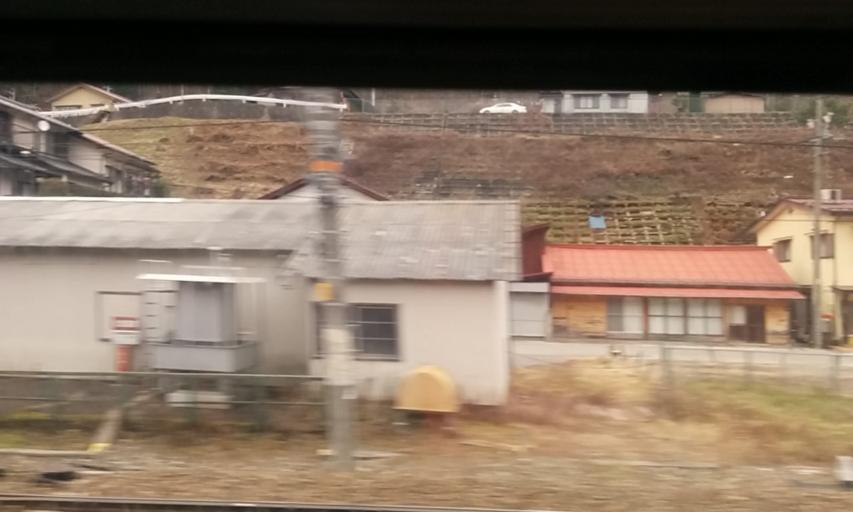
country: JP
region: Nagano
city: Ina
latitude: 35.9322
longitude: 137.7852
